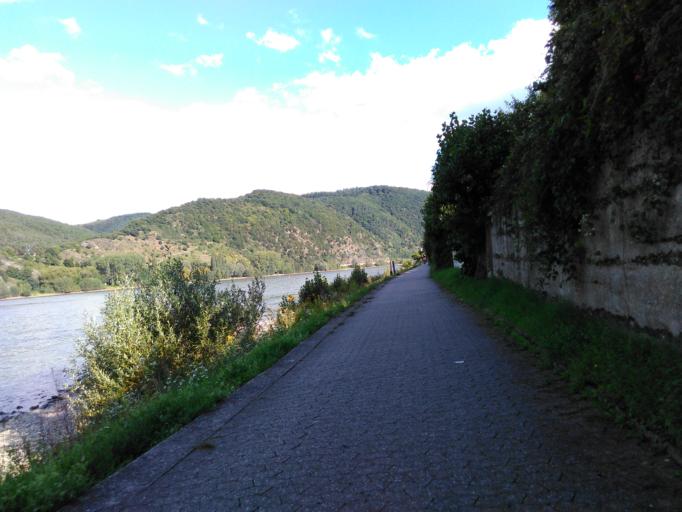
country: DE
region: Rheinland-Pfalz
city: Braubach
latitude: 50.2688
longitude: 7.6411
